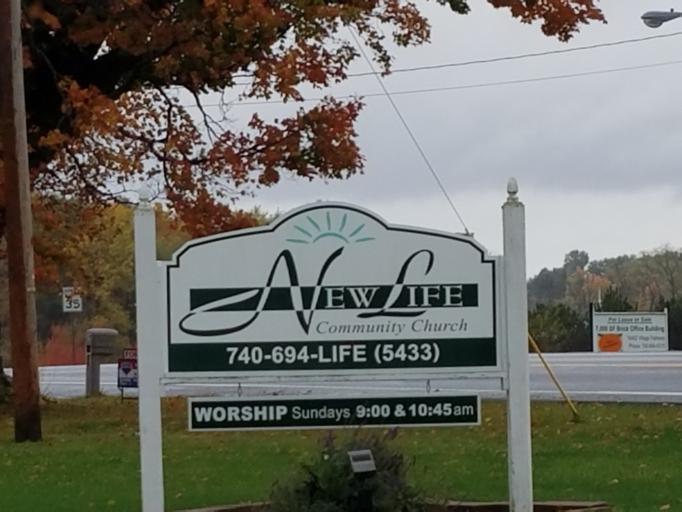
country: US
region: Ohio
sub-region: Knox County
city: Fredericktown
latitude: 40.4775
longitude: -82.5611
